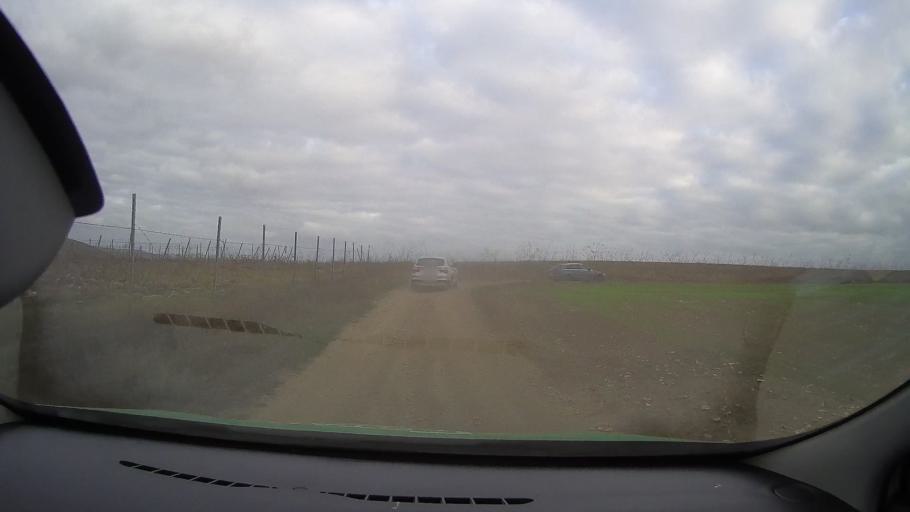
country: RO
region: Tulcea
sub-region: Comuna Jurilovca
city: Jurilovca
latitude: 44.7696
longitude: 28.9067
